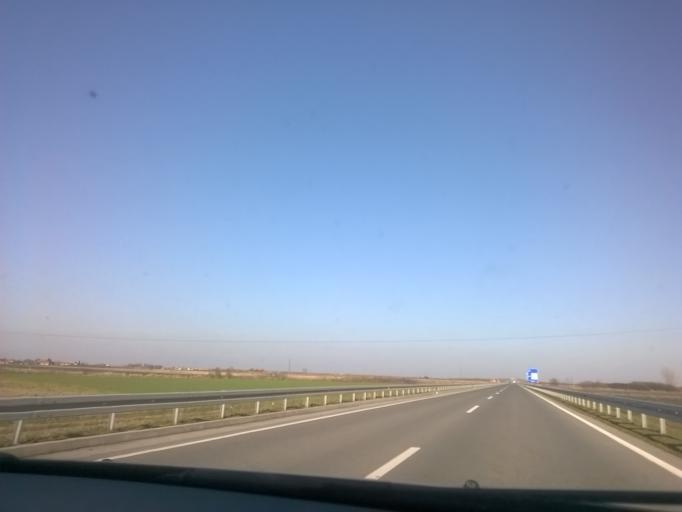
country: RS
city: Pavlis
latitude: 45.1005
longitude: 21.2613
